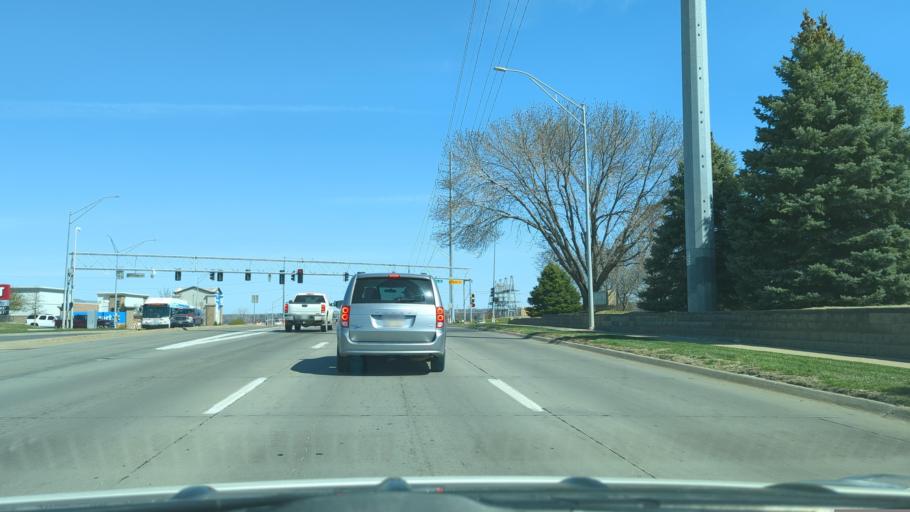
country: US
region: Nebraska
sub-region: Douglas County
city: Ralston
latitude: 41.2425
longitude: -96.0239
